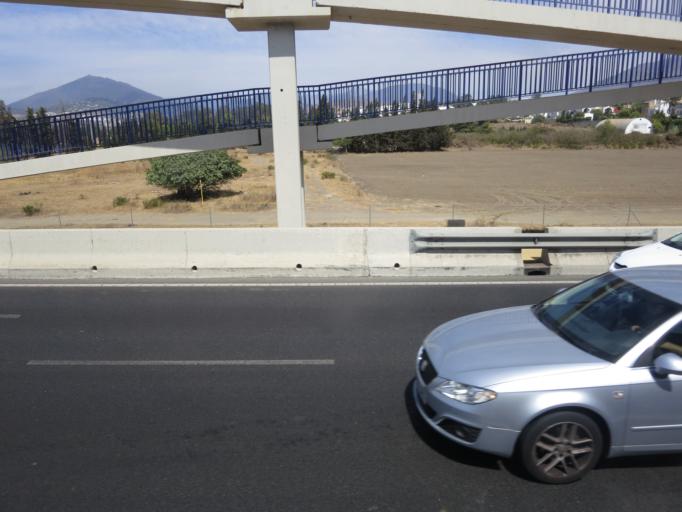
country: ES
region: Andalusia
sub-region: Provincia de Malaga
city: Benahavis
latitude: 36.4857
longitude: -4.9742
